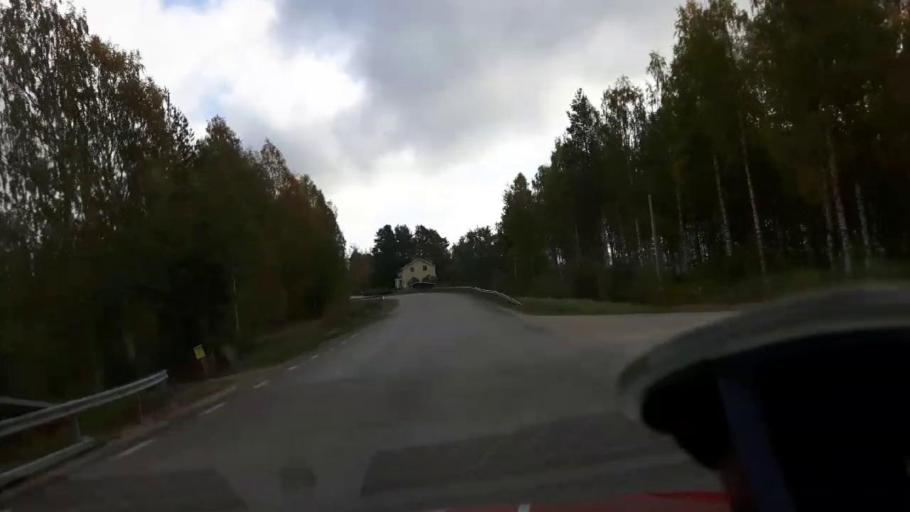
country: SE
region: Gaevleborg
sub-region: Ljusdals Kommun
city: Farila
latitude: 61.7850
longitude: 15.9303
